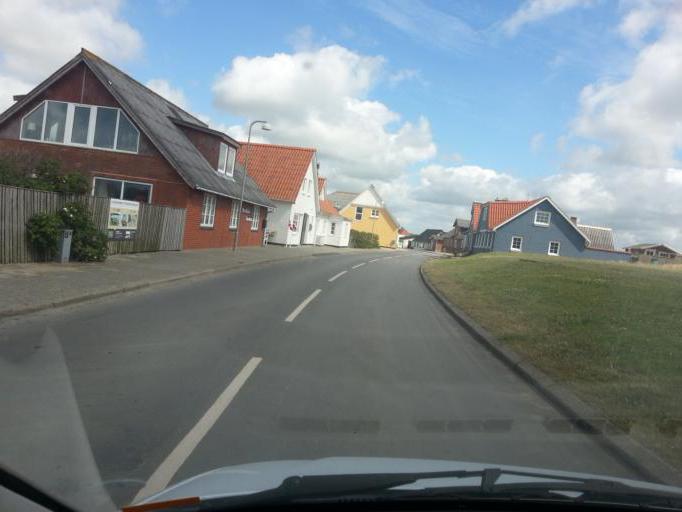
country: DK
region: Central Jutland
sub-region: Lemvig Kommune
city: Harboore
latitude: 56.5258
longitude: 8.1214
